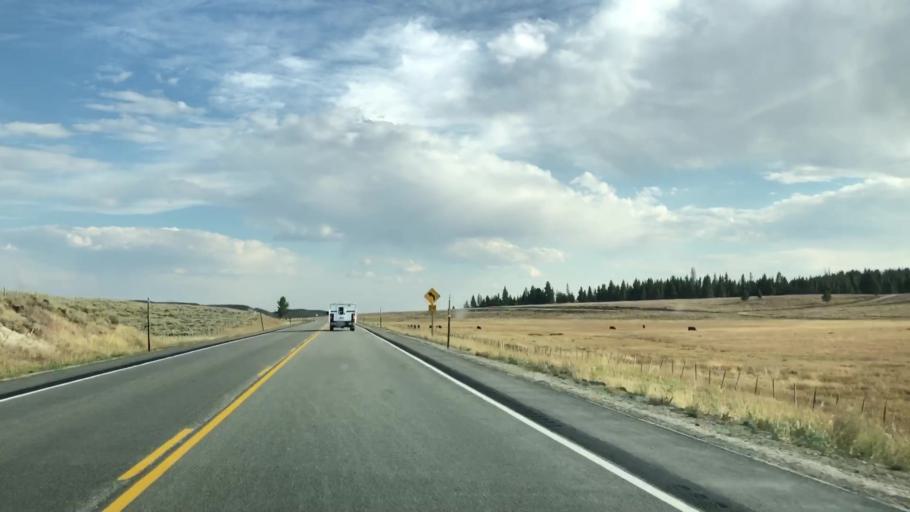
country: US
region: Wyoming
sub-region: Sublette County
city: Pinedale
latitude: 43.1291
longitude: -110.1909
